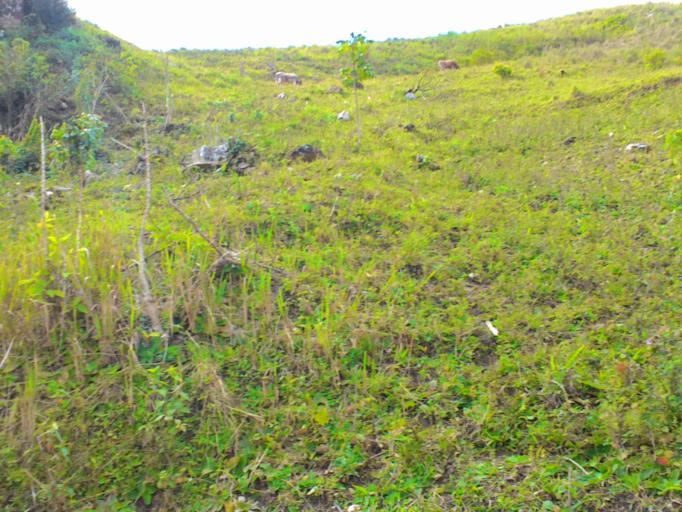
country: HT
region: Sud
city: Les Anglais
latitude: 18.4491
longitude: -74.1048
